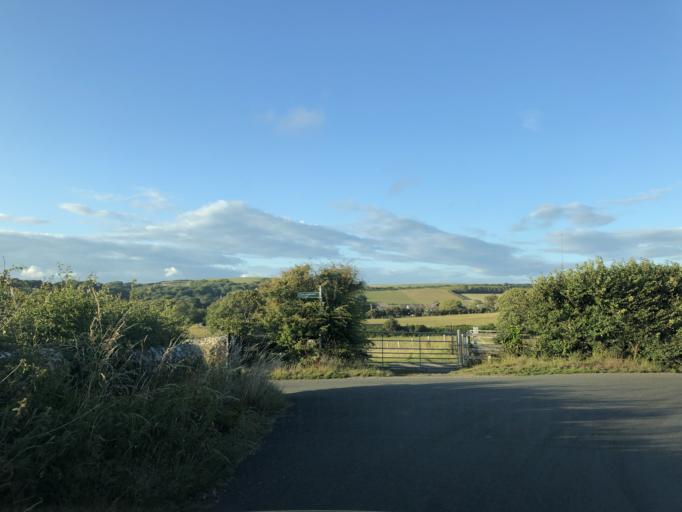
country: GB
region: England
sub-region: Isle of Wight
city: Chale
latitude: 50.6389
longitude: -1.3598
